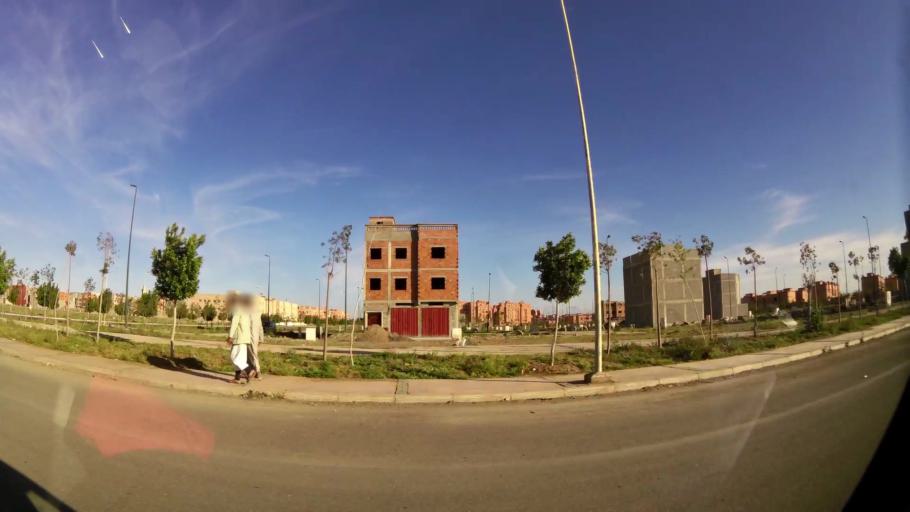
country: MA
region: Marrakech-Tensift-Al Haouz
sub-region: Marrakech
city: Marrakesh
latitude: 31.7601
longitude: -8.1049
